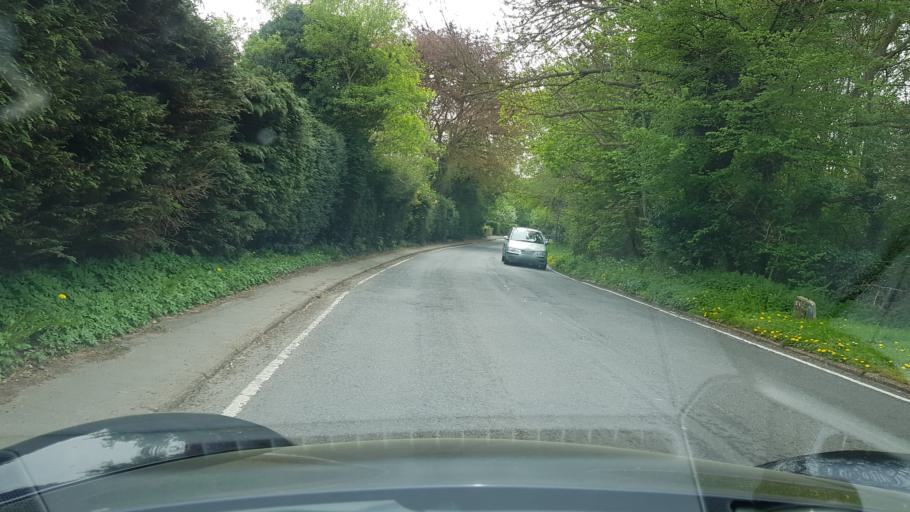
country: GB
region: England
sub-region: Surrey
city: East Horsley
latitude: 51.2634
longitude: -0.4565
